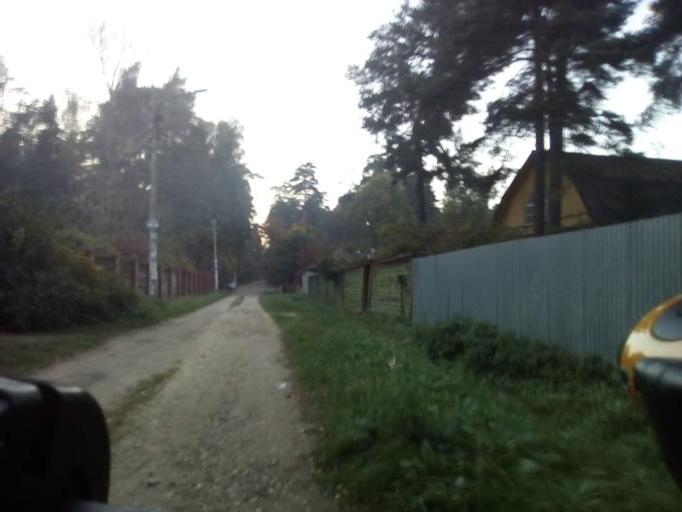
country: RU
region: Moskovskaya
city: Kratovo
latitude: 55.5970
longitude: 38.1857
